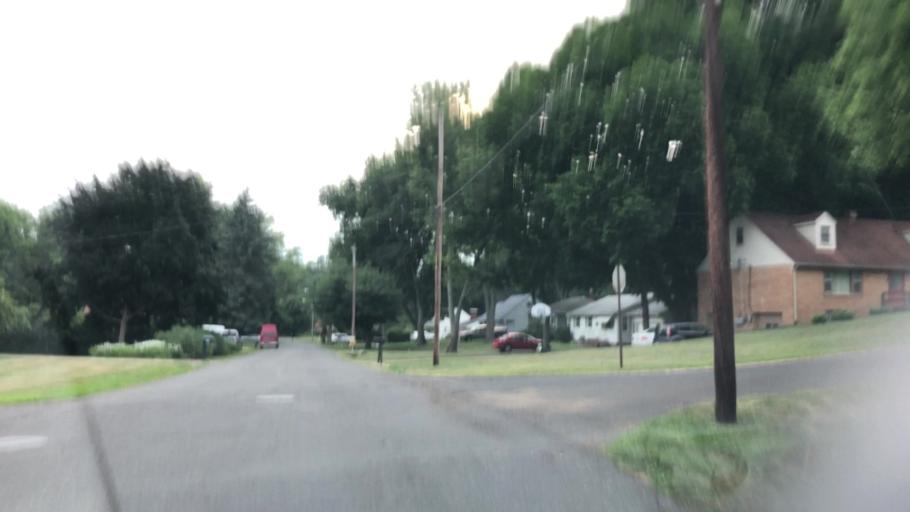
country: US
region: Ohio
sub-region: Stark County
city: North Canton
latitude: 40.8527
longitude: -81.3860
